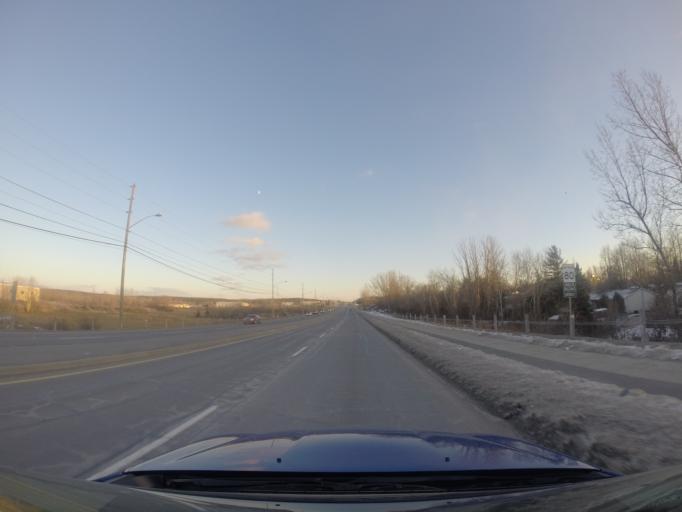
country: CA
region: Ontario
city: Greater Sudbury
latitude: 46.5031
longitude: -80.9333
